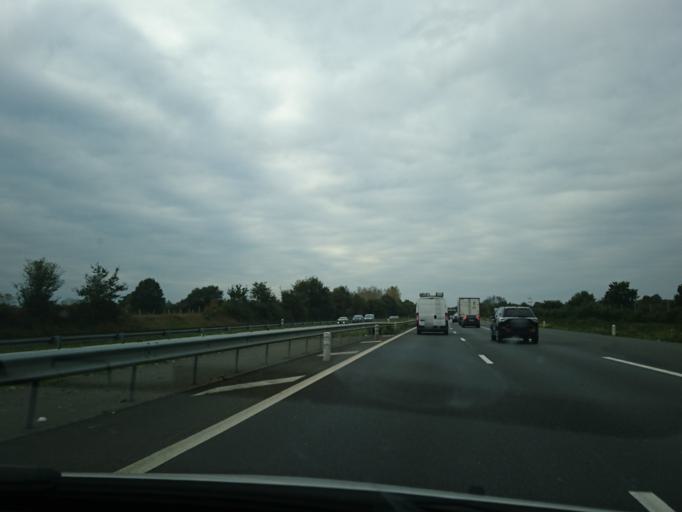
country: FR
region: Pays de la Loire
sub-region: Departement de la Loire-Atlantique
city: Sautron
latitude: 47.2662
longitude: -1.7094
